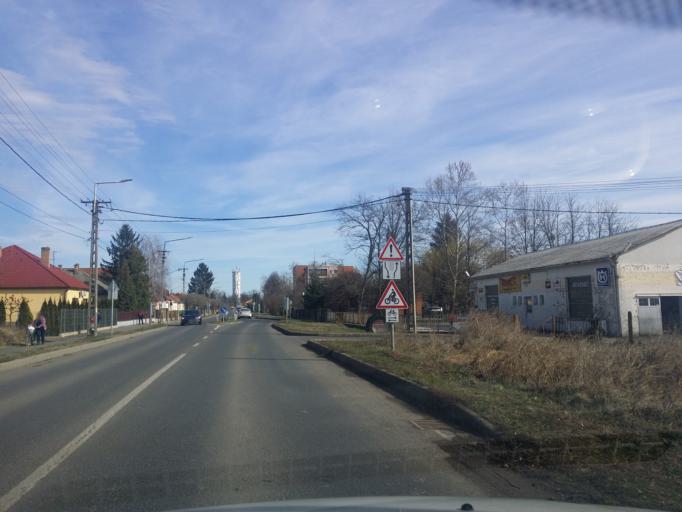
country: HU
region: Baranya
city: Mohacs
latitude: 45.9967
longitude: 18.6708
